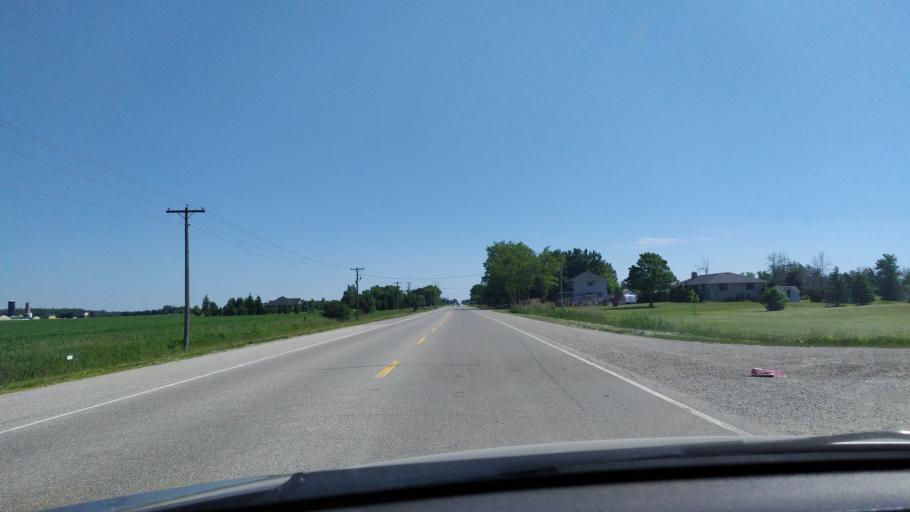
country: CA
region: Ontario
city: Stratford
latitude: 43.3960
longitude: -80.9623
